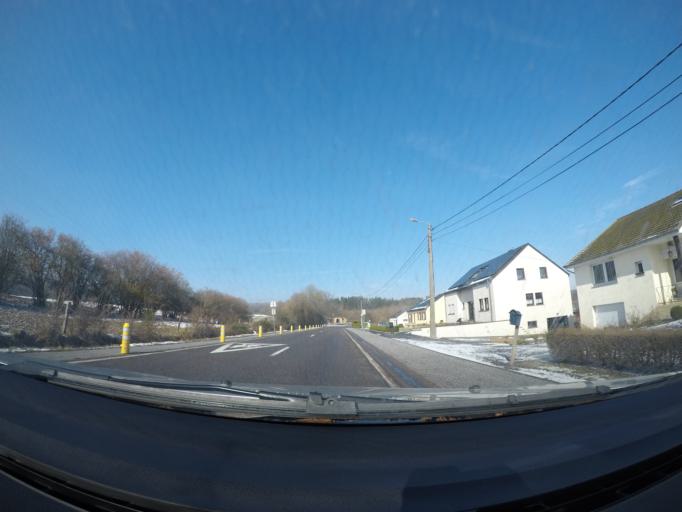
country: BE
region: Wallonia
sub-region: Province du Luxembourg
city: Tintigny
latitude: 49.7310
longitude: 5.5288
